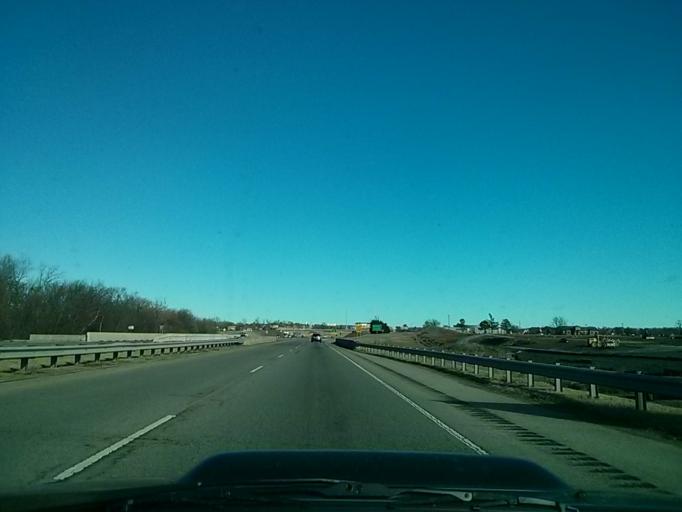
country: US
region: Oklahoma
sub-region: Tulsa County
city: Jenks
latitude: 36.0203
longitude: -96.0114
